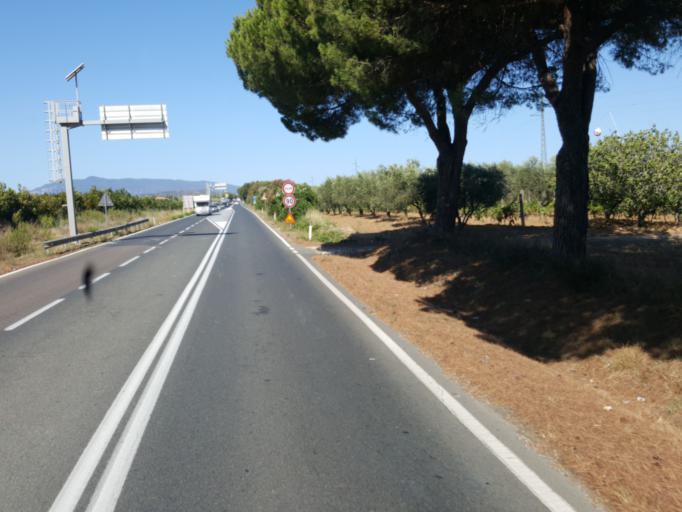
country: IT
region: Tuscany
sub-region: Provincia di Grosseto
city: Capalbio
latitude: 42.4151
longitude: 11.3717
